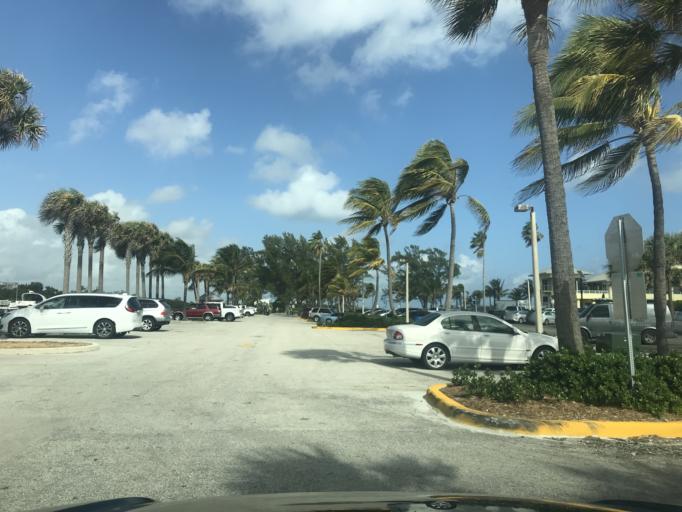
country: US
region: Florida
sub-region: Broward County
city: Dania Beach
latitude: 26.0576
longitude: -80.1123
